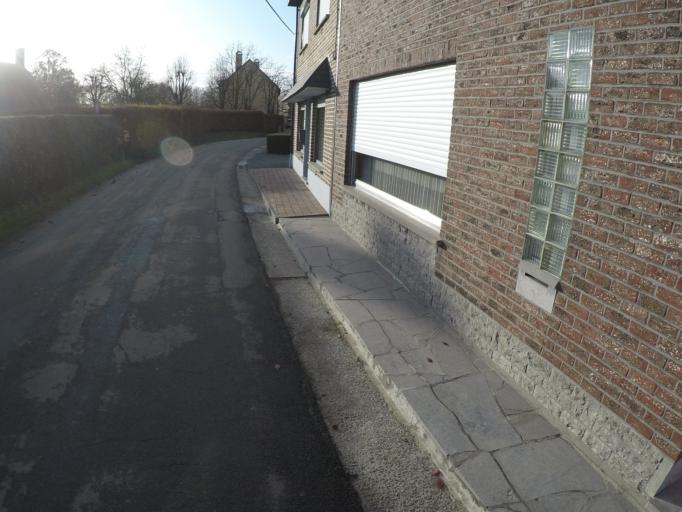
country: BE
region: Flanders
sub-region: Provincie Vlaams-Brabant
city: Opwijk
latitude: 50.9588
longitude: 4.1873
